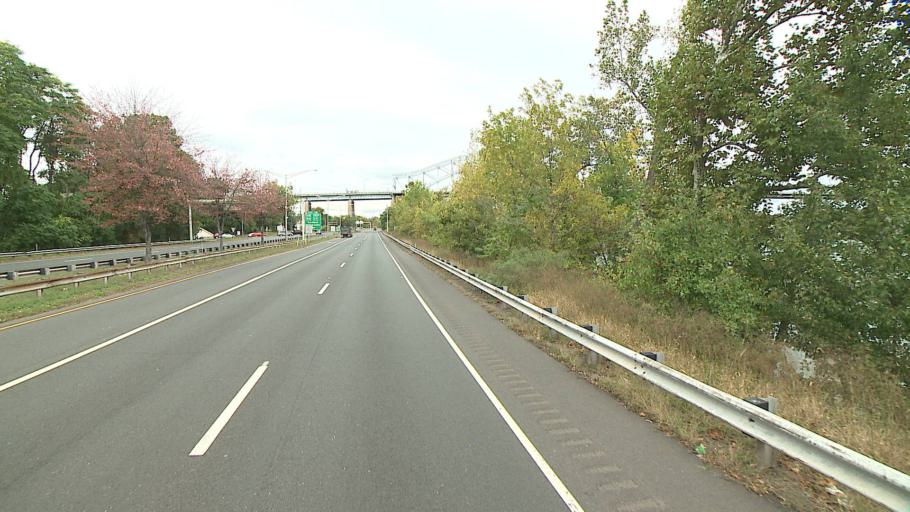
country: US
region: Connecticut
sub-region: Middlesex County
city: Middletown
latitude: 41.5666
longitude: -72.6498
